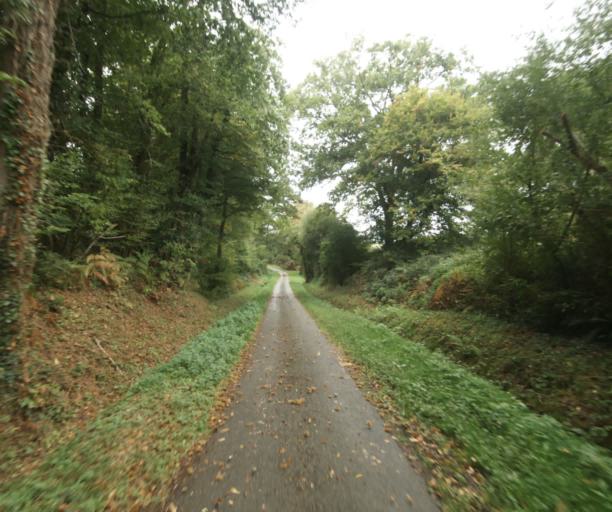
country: FR
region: Midi-Pyrenees
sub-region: Departement du Gers
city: Cazaubon
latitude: 43.8961
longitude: -0.1109
